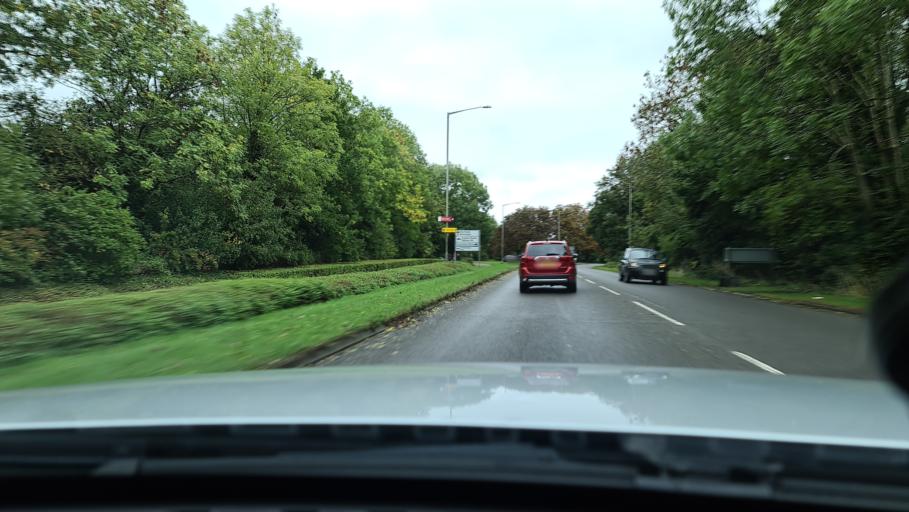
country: GB
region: England
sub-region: Milton Keynes
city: Stony Stratford
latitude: 52.0512
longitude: -0.8416
